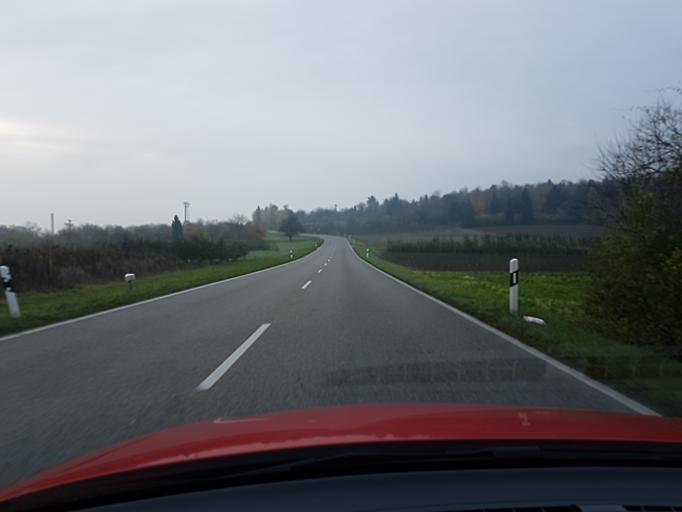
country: DE
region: Baden-Wuerttemberg
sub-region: Regierungsbezirk Stuttgart
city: Gemmrigheim
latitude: 49.0296
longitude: 9.1476
